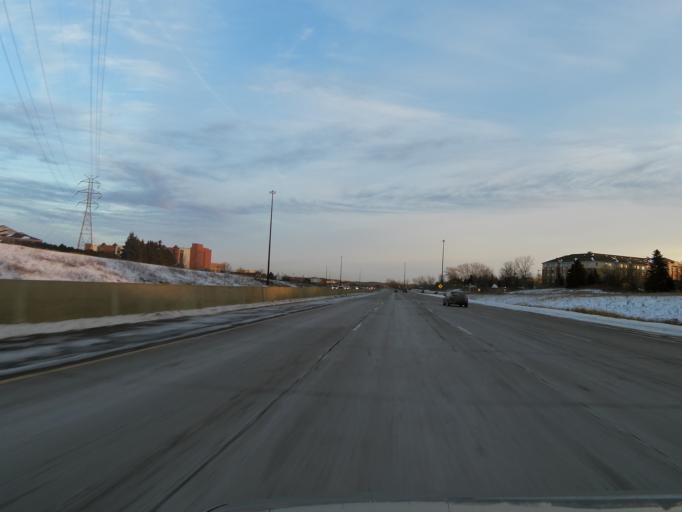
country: US
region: Minnesota
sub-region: Hennepin County
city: Eden Prairie
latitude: 44.8623
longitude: -93.4246
